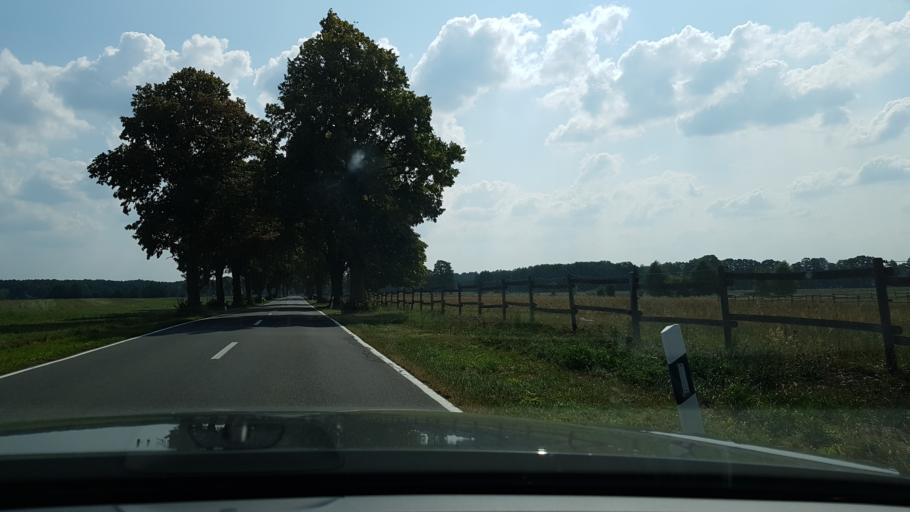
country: DE
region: Brandenburg
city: Lindow
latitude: 53.0215
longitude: 12.9748
